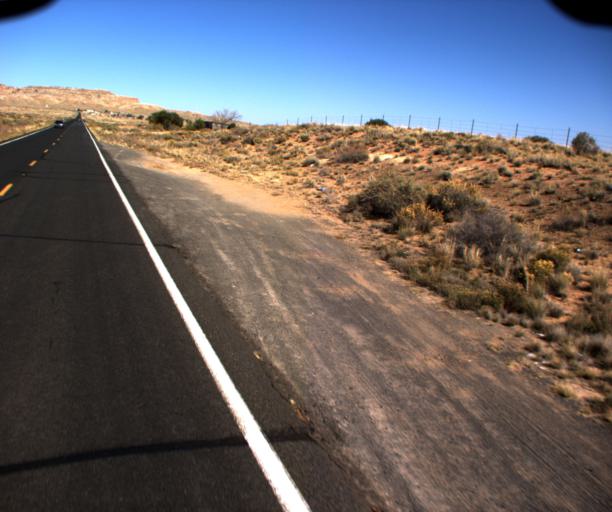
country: US
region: Arizona
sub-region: Navajo County
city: First Mesa
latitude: 35.7697
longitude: -110.5066
